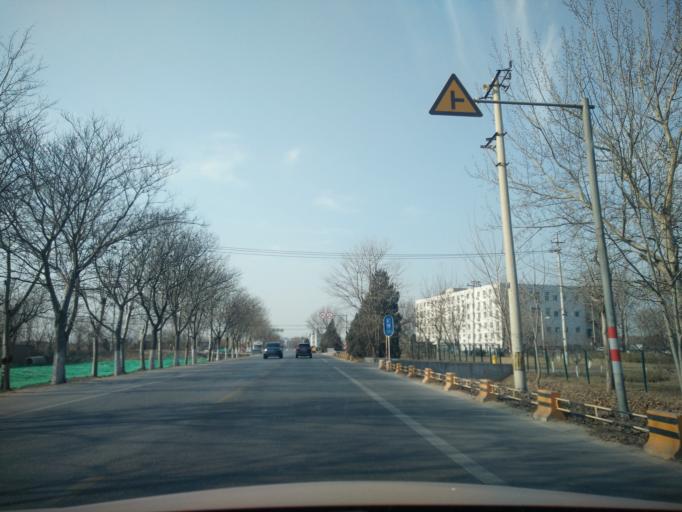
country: CN
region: Beijing
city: Yinghai
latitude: 39.7649
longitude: 116.4701
